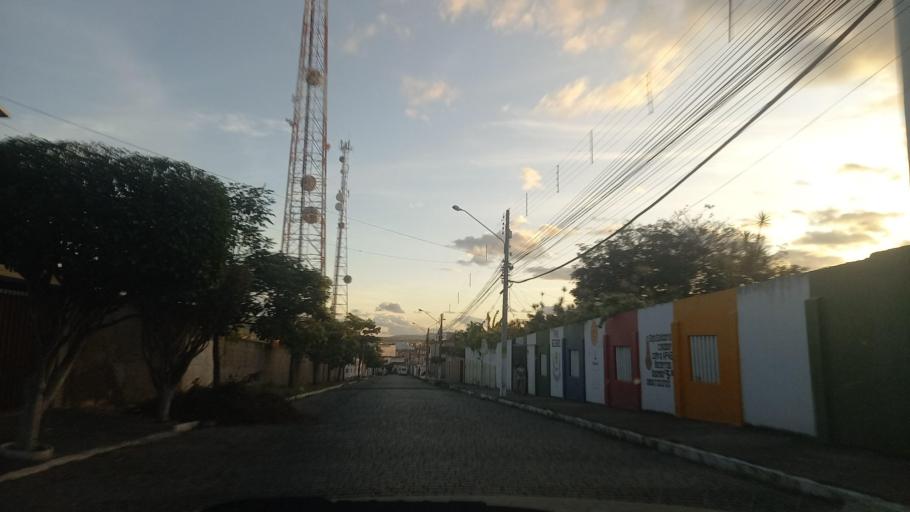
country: BR
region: Pernambuco
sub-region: Bezerros
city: Bezerros
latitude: -8.2420
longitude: -35.7526
